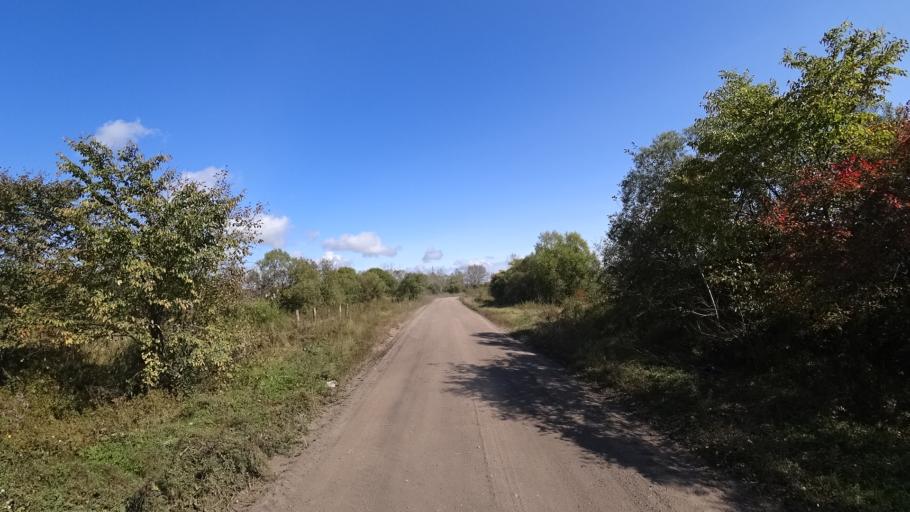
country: RU
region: Amur
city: Arkhara
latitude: 49.4064
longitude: 130.1575
